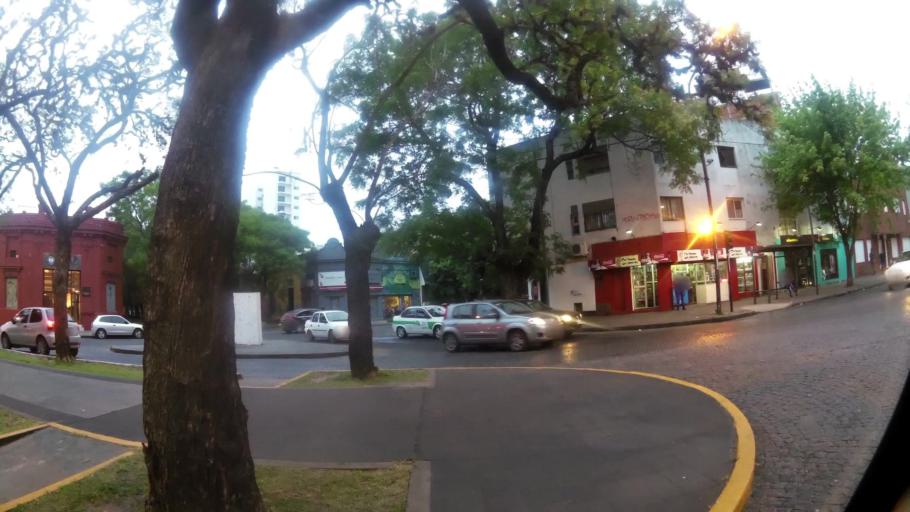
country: AR
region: Buenos Aires
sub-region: Partido de La Plata
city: La Plata
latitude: -34.9217
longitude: -57.9612
